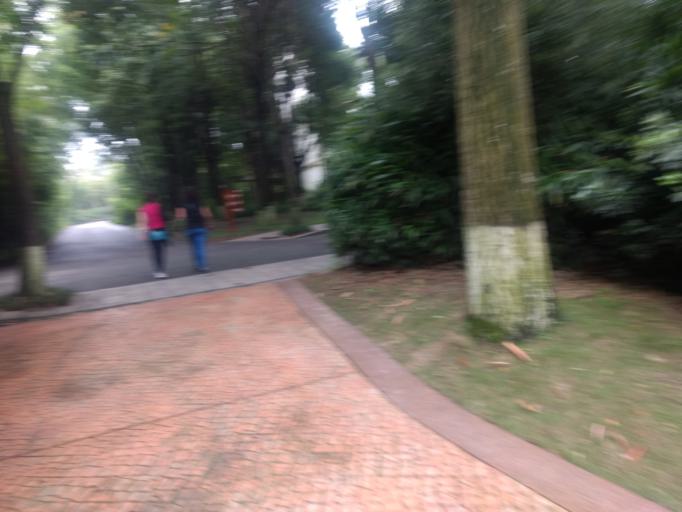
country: CN
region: Sichuan
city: Xindu
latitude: 30.7367
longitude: 104.1445
